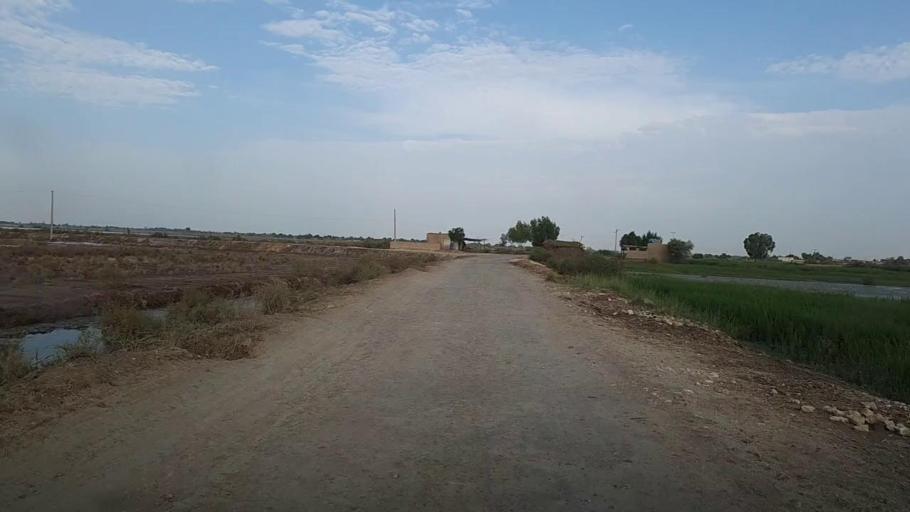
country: PK
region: Sindh
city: Thul
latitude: 28.2635
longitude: 68.8657
